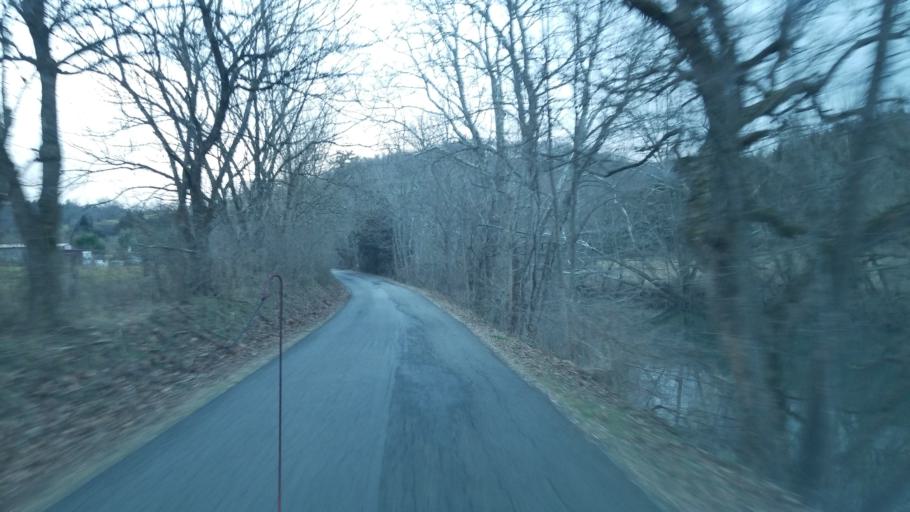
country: US
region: Virginia
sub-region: Pulaski County
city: Pulaski
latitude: 37.1611
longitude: -80.8648
